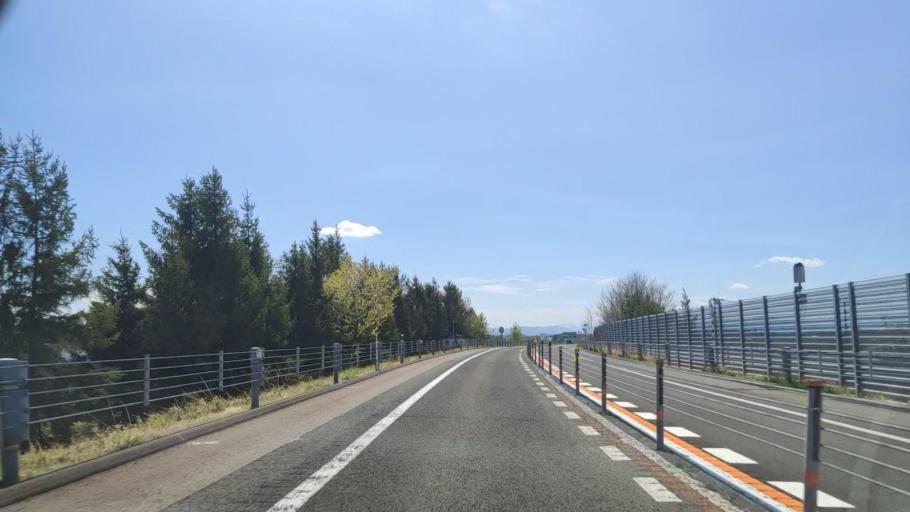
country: JP
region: Akita
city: Yokotemachi
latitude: 39.3443
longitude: 140.5000
